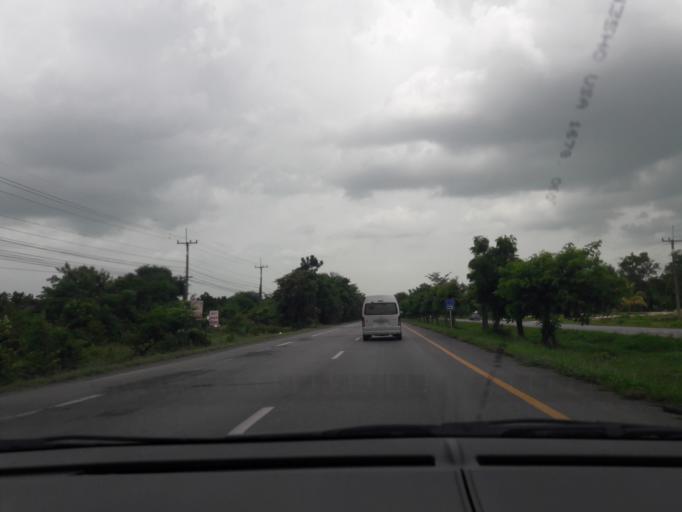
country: TH
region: Nakhon Ratchasima
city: Non Sung
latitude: 15.0982
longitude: 102.2599
